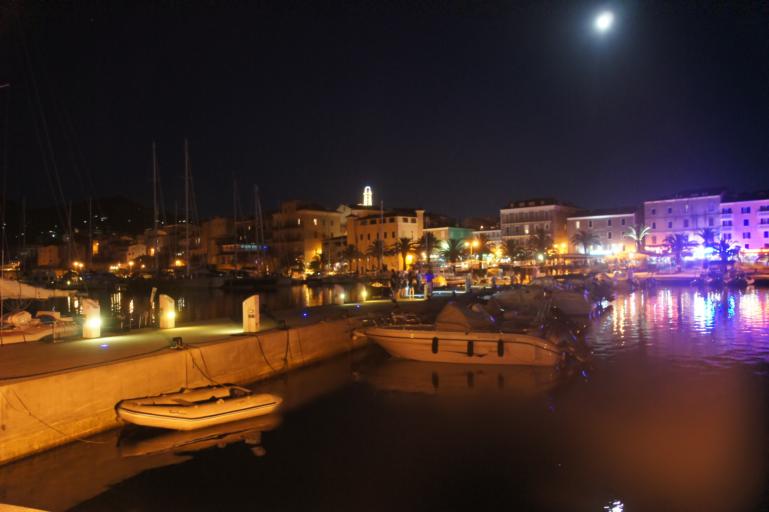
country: FR
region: Corsica
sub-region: Departement de la Corse-du-Sud
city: Propriano
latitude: 41.6763
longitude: 8.9024
